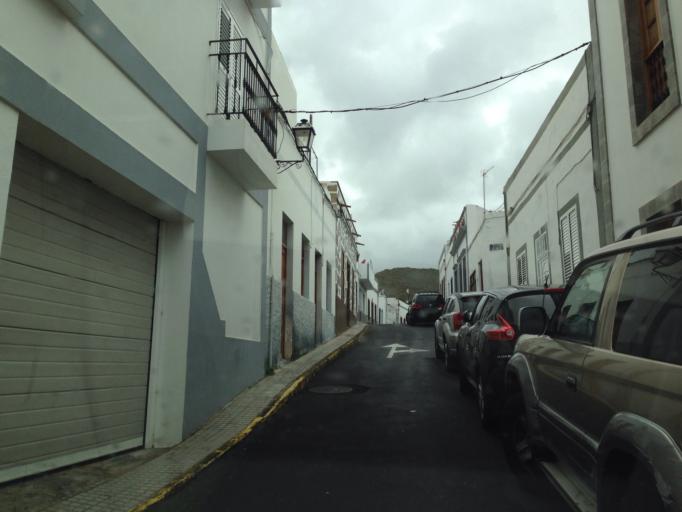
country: ES
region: Canary Islands
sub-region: Provincia de Las Palmas
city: Agaete
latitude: 28.0988
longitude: -15.6988
